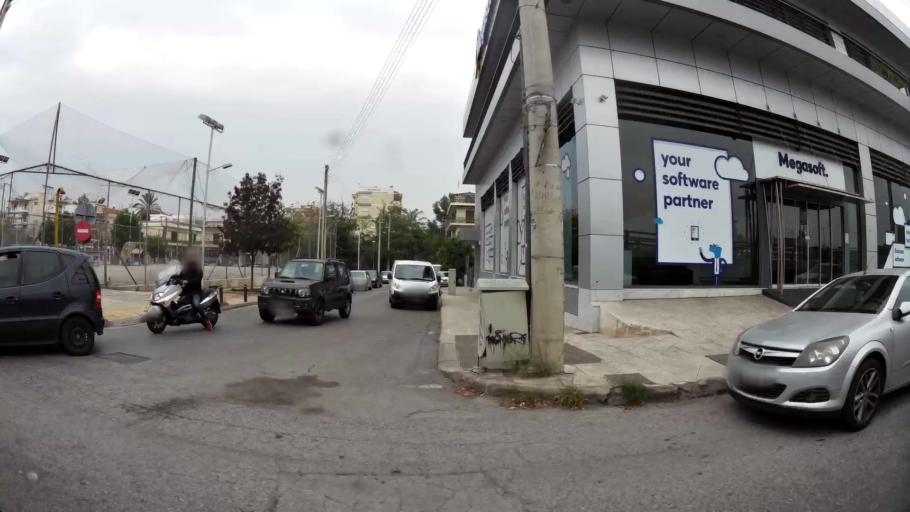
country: GR
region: Attica
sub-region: Nomarchia Athinas
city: Aigaleo
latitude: 37.9951
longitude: 23.6927
